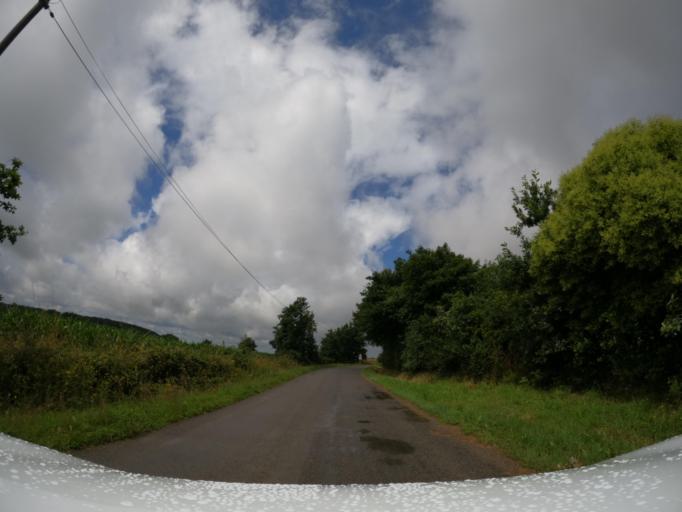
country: FR
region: Pays de la Loire
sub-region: Departement de la Loire-Atlantique
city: Ligne
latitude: 47.3978
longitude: -1.3863
